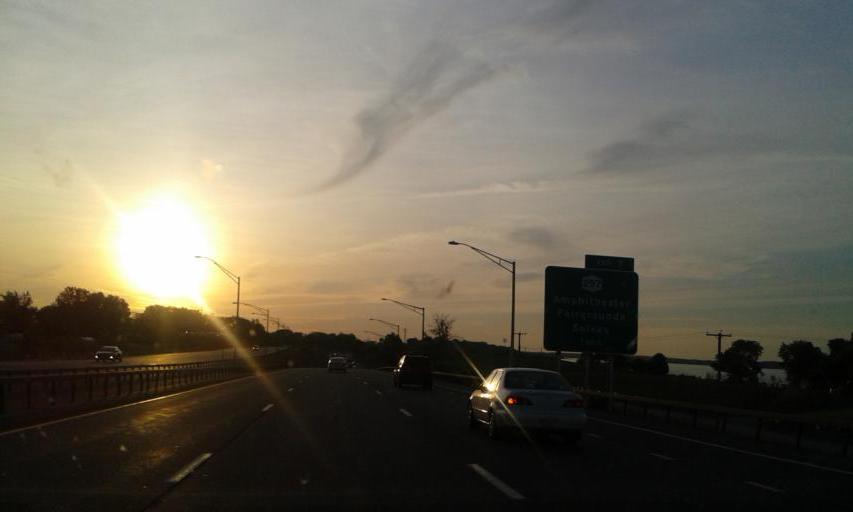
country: US
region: New York
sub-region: Onondaga County
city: Solvay
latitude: 43.0618
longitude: -76.1898
